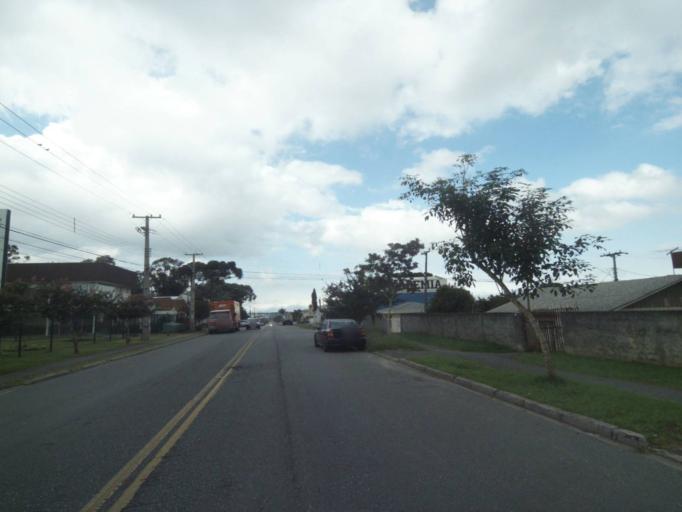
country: BR
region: Parana
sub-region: Pinhais
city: Pinhais
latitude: -25.4522
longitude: -49.2129
